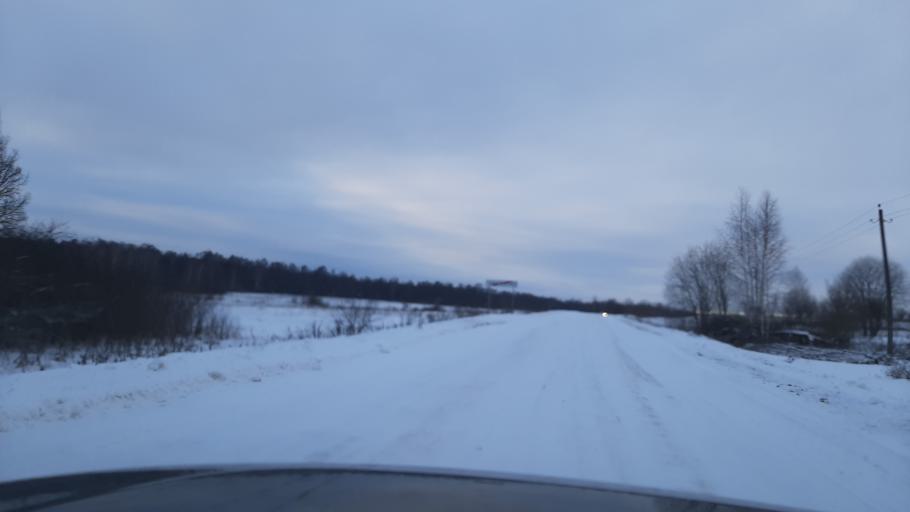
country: RU
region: Kostroma
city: Volgorechensk
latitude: 57.4469
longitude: 40.9663
